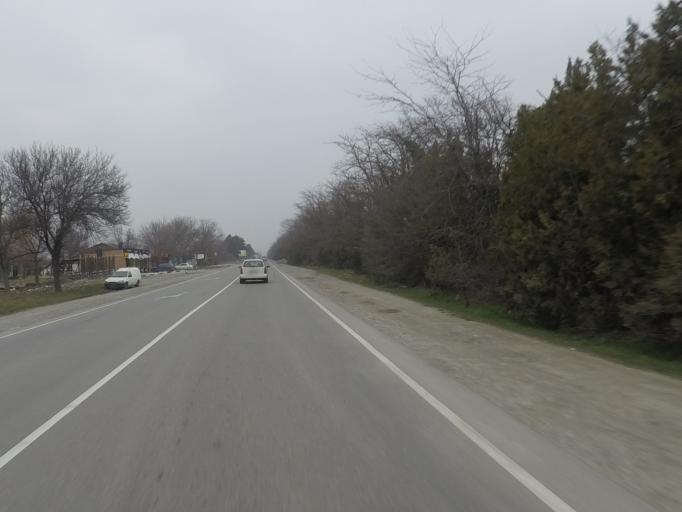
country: GE
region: Mtskheta-Mtianeti
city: Mtskheta
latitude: 41.8959
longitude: 44.7192
